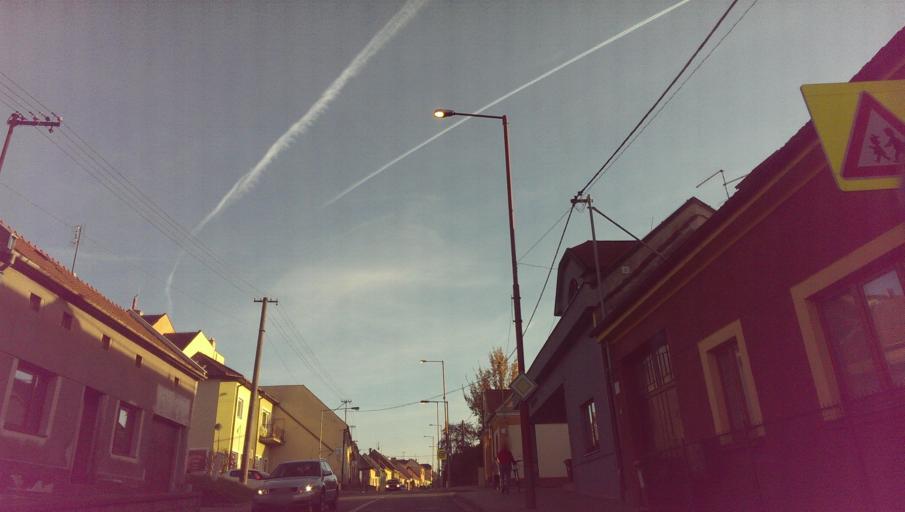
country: CZ
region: Zlin
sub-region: Okres Uherske Hradiste
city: Uherske Hradiste
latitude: 49.0658
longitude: 17.4801
